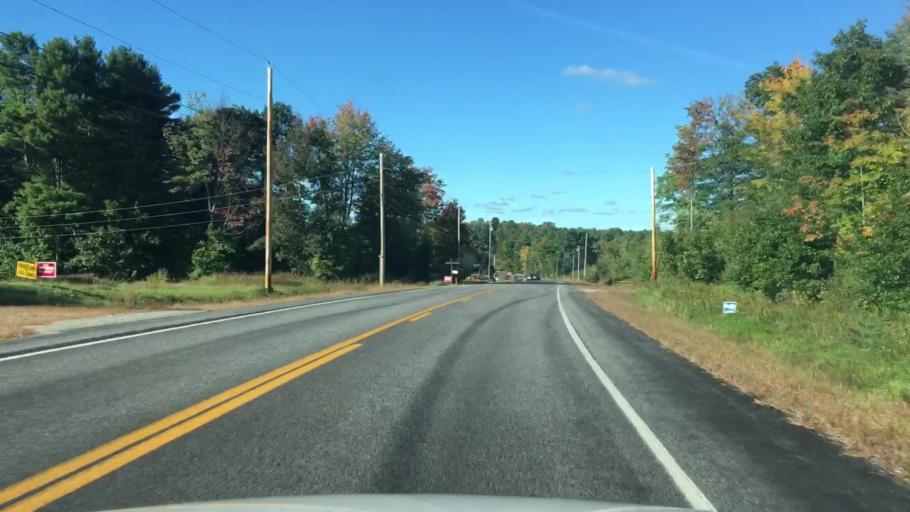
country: US
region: Maine
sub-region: Androscoggin County
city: Lisbon
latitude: 44.0440
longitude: -70.0772
